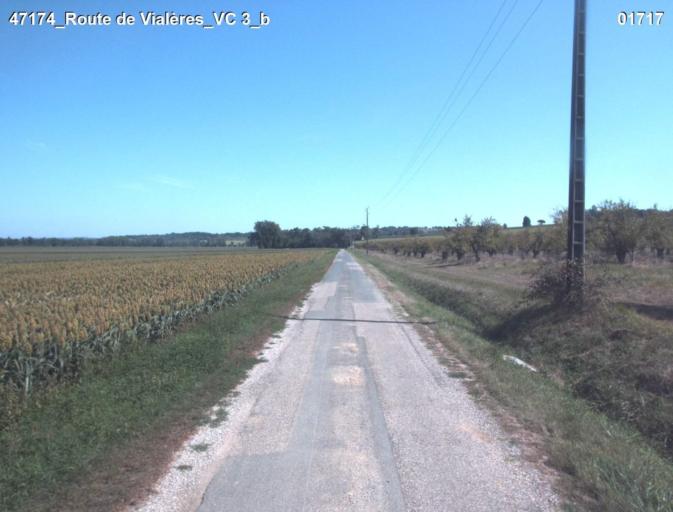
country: FR
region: Aquitaine
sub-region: Departement du Lot-et-Garonne
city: Nerac
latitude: 44.0485
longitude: 0.3808
